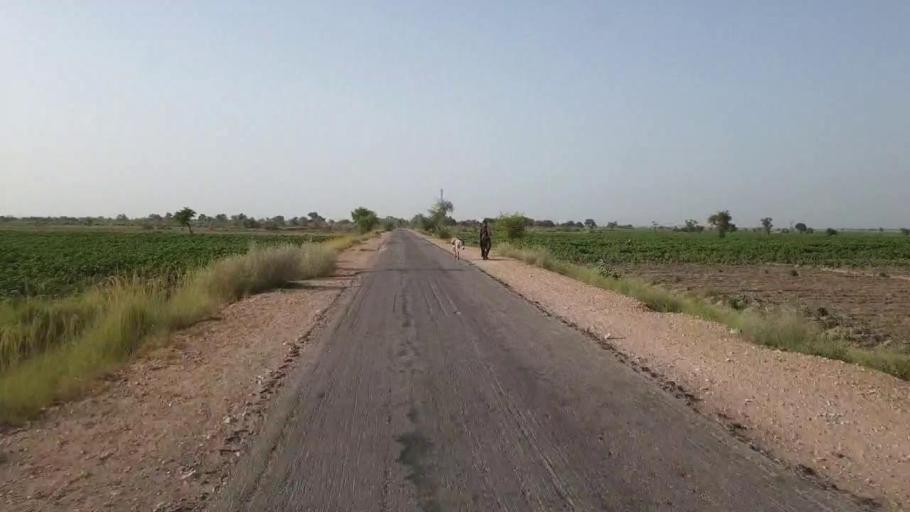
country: PK
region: Sindh
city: Jam Sahib
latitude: 26.4754
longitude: 68.8598
